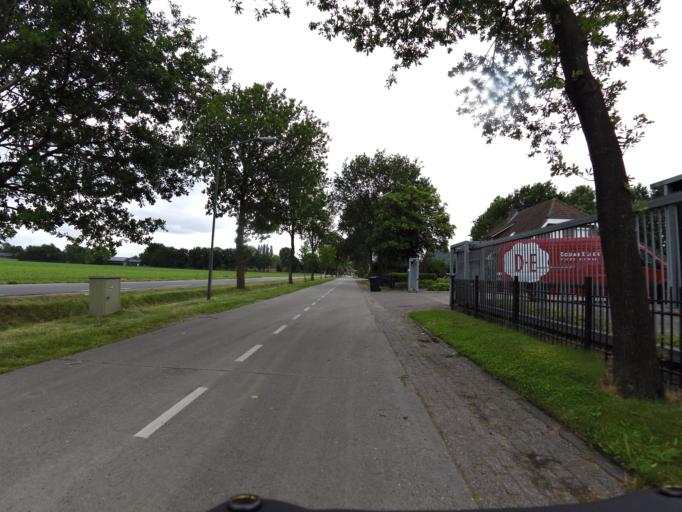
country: BE
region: Flanders
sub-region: Provincie Antwerpen
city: Baarle-Hertog
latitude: 51.4598
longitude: 4.8494
